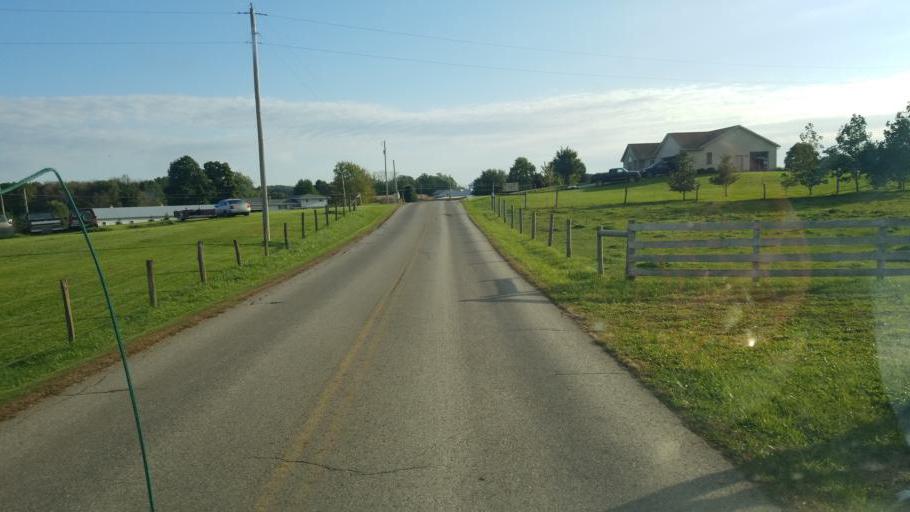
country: US
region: Ohio
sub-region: Wayne County
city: Shreve
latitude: 40.6312
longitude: -82.0814
